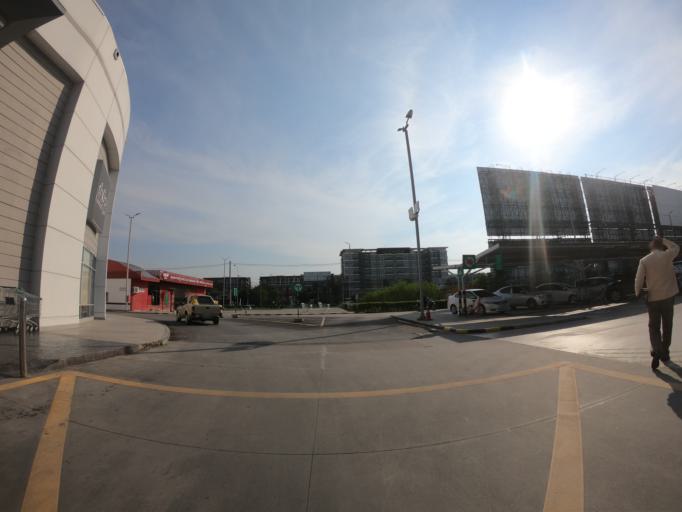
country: TH
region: Chiang Mai
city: San Sai
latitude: 18.8239
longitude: 99.0133
